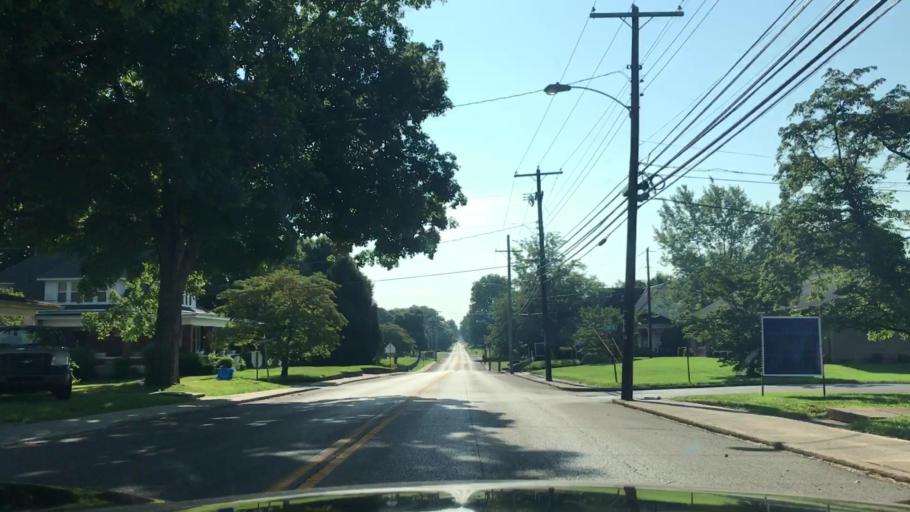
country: US
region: Kentucky
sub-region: Hart County
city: Horse Cave
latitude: 37.1789
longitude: -85.9006
